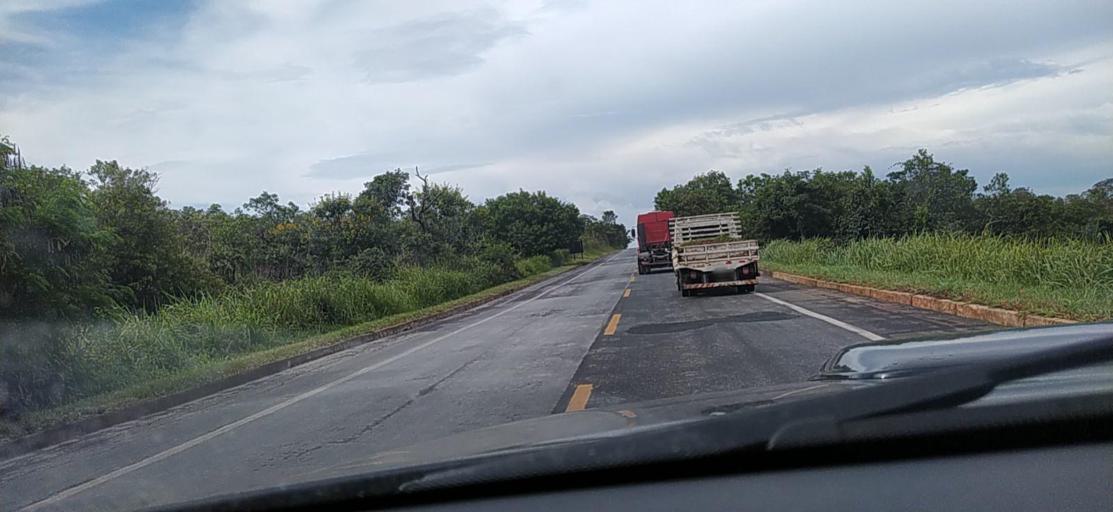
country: BR
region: Minas Gerais
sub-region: Montes Claros
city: Montes Claros
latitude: -16.8522
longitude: -43.8524
